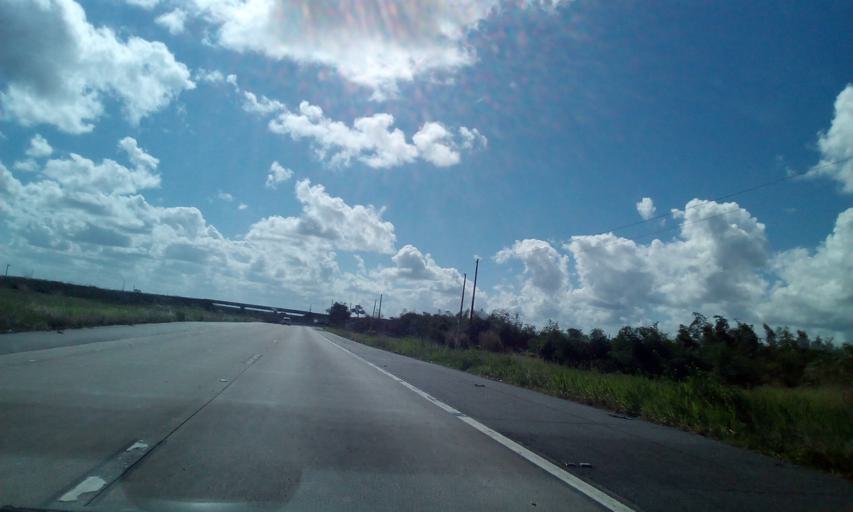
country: BR
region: Pernambuco
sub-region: Goiana
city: Goiana
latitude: -7.6335
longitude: -34.9610
